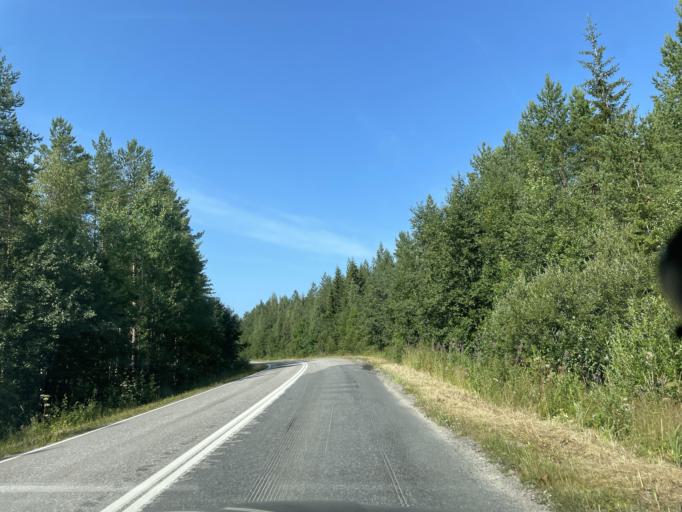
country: FI
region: Central Finland
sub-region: Saarijaervi-Viitasaari
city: Pihtipudas
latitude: 63.3655
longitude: 25.7116
